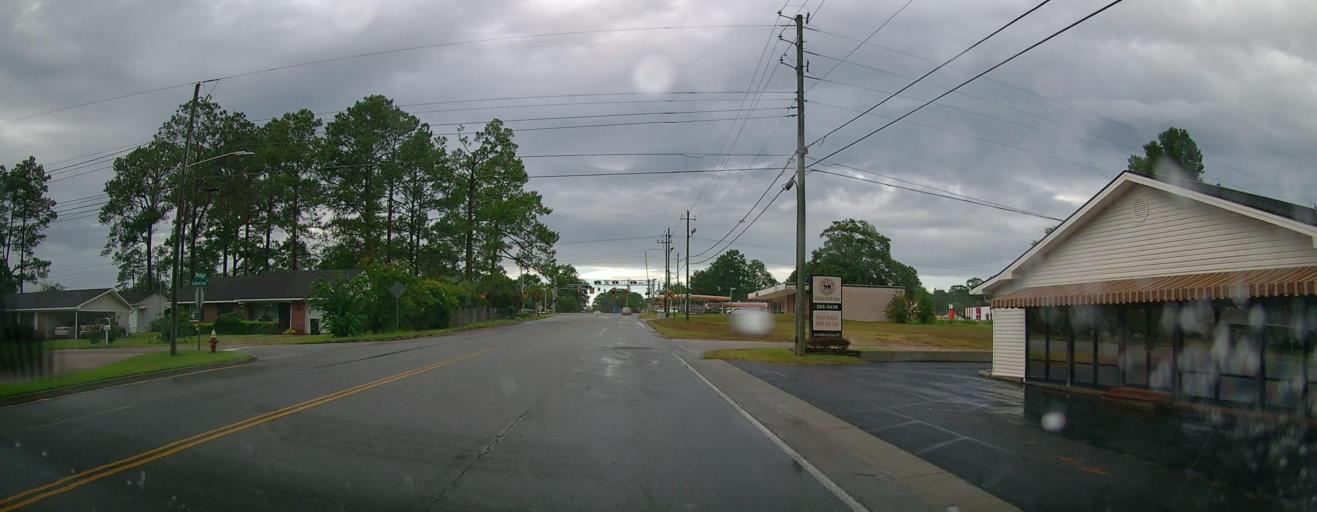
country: US
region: Georgia
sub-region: Ware County
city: Sunnyside
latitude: 31.2289
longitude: -82.3316
